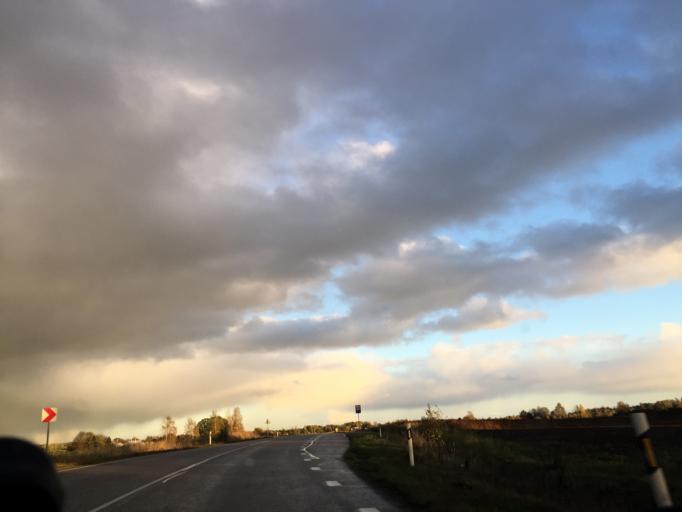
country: LV
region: Talsu Rajons
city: Sabile
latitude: 56.9313
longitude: 22.5332
